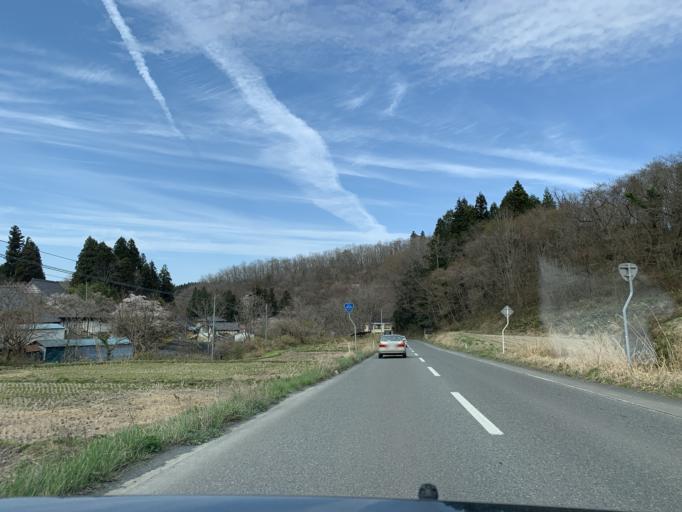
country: JP
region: Iwate
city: Ichinoseki
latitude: 38.8414
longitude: 141.3408
